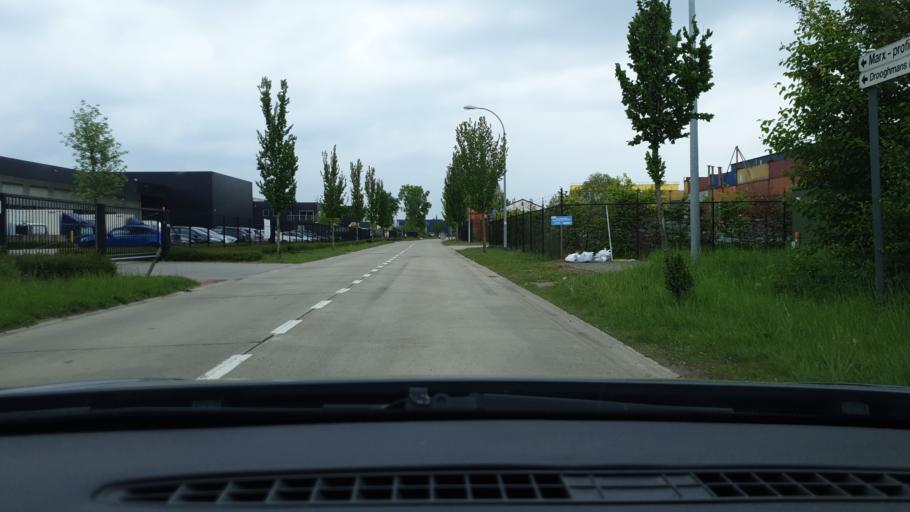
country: BE
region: Flanders
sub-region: Provincie Antwerpen
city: Balen
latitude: 51.1545
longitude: 5.1534
